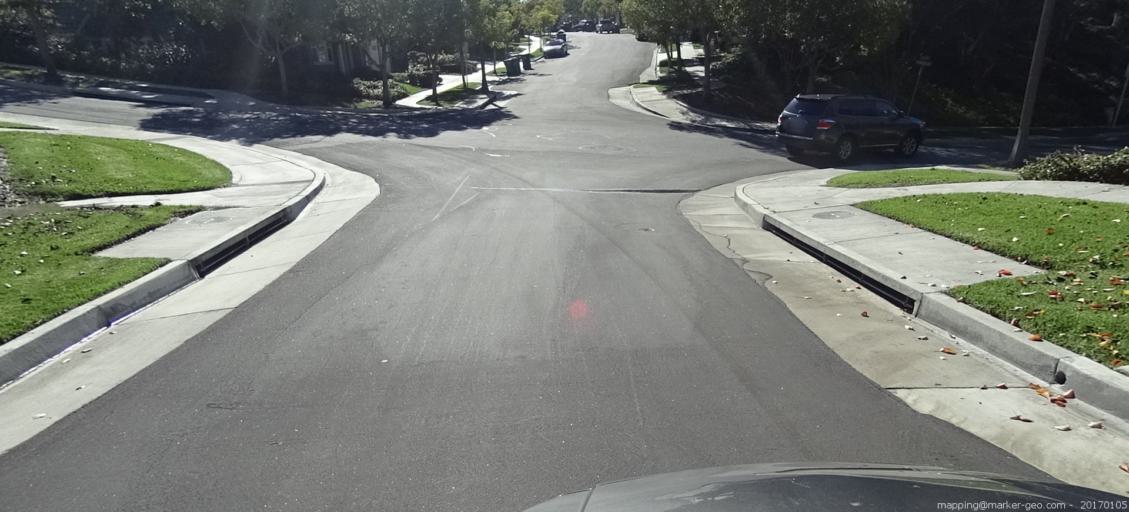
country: US
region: California
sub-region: Orange County
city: Ladera Ranch
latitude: 33.5497
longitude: -117.6307
